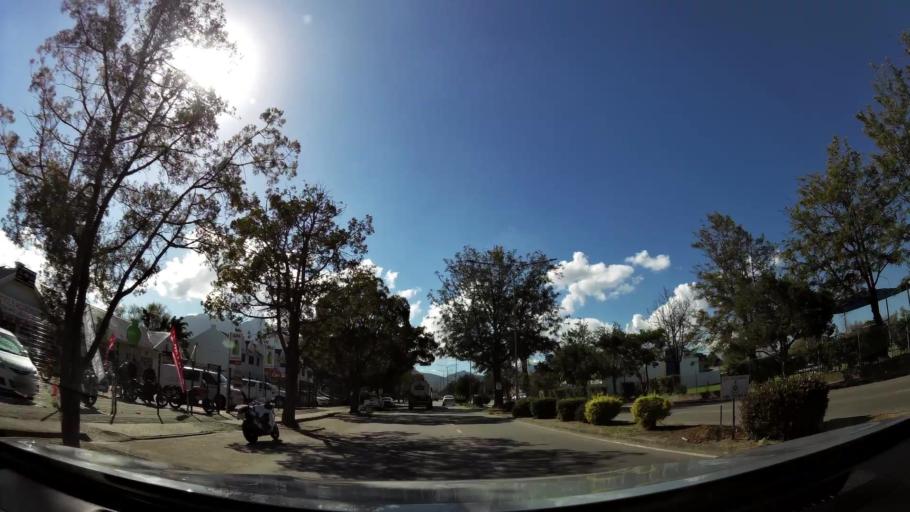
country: ZA
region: Western Cape
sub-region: Eden District Municipality
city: George
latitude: -33.9691
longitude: 22.4487
